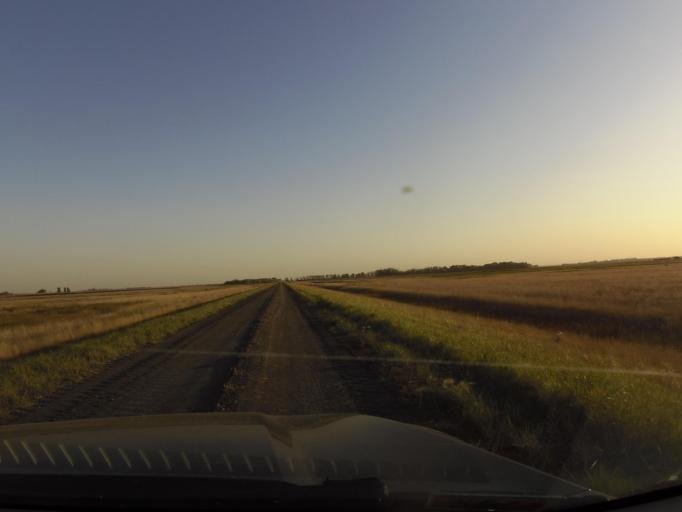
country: US
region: North Dakota
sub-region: Walsh County
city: Grafton
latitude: 48.4185
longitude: -97.4704
